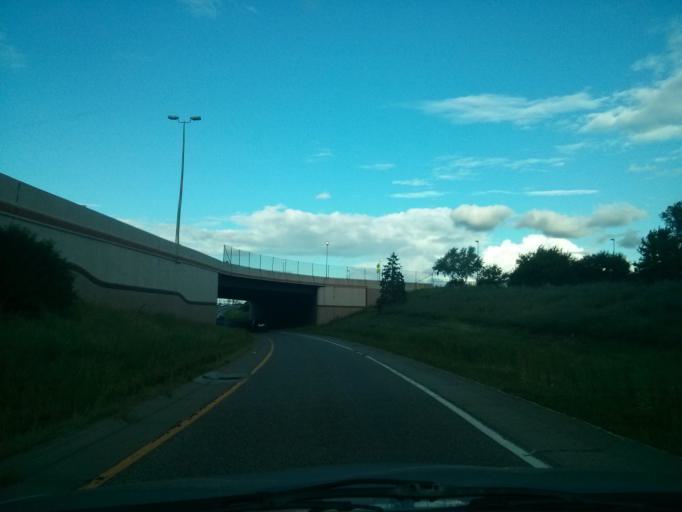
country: US
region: Minnesota
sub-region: Hennepin County
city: Richfield
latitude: 44.8618
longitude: -93.2395
